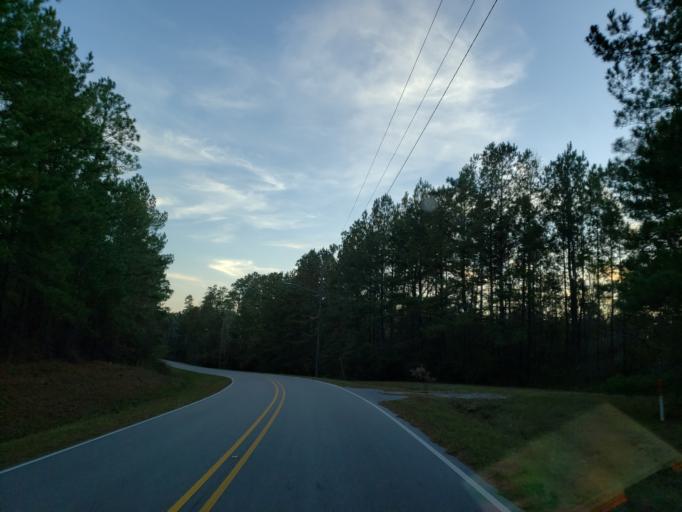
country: US
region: Mississippi
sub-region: Forrest County
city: Hattiesburg
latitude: 31.2721
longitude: -89.3097
